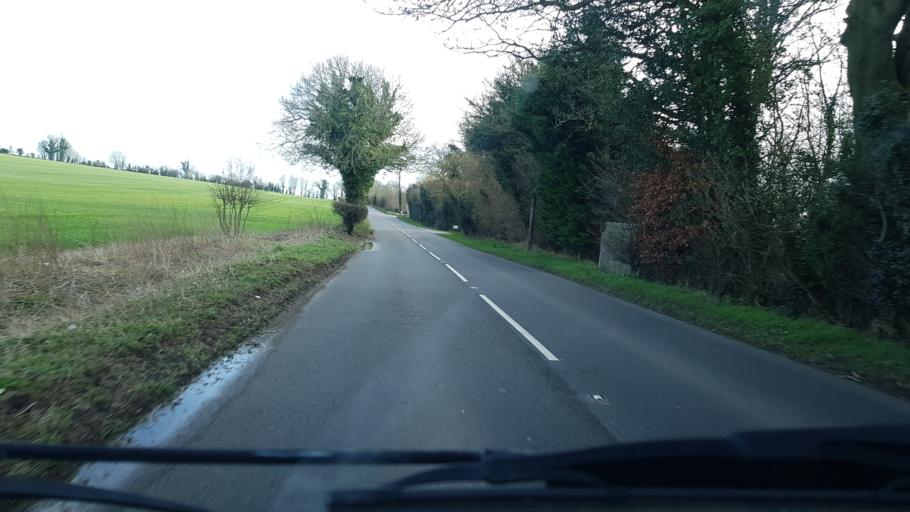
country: GB
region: England
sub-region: Wiltshire
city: Avebury
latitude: 51.4560
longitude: -1.8573
